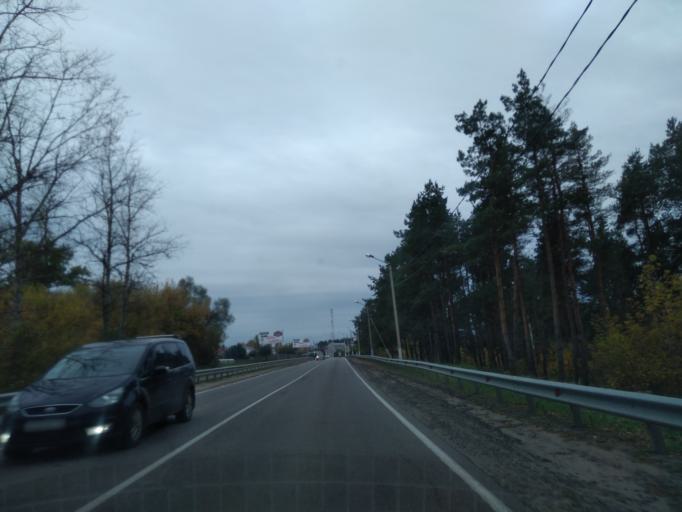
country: RU
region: Lipetsk
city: Zadonsk
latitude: 52.3853
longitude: 38.9373
